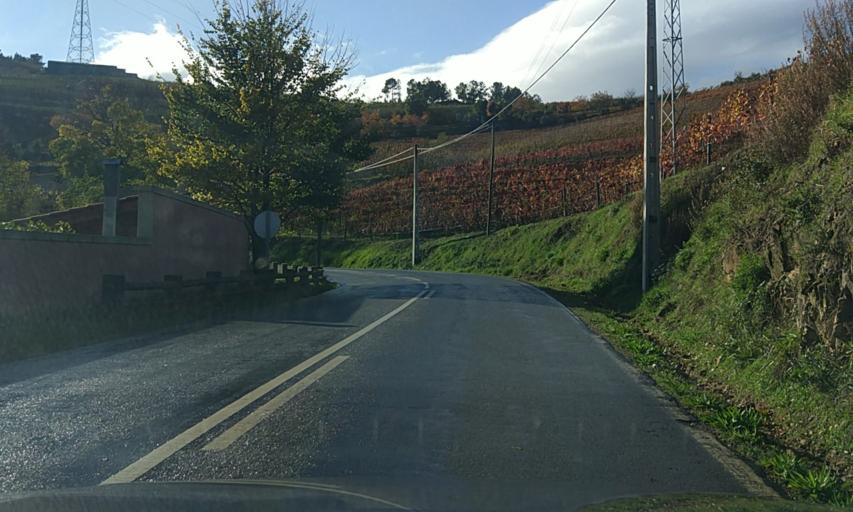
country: PT
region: Viseu
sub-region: Lamego
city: Lamego
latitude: 41.1201
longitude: -7.7945
